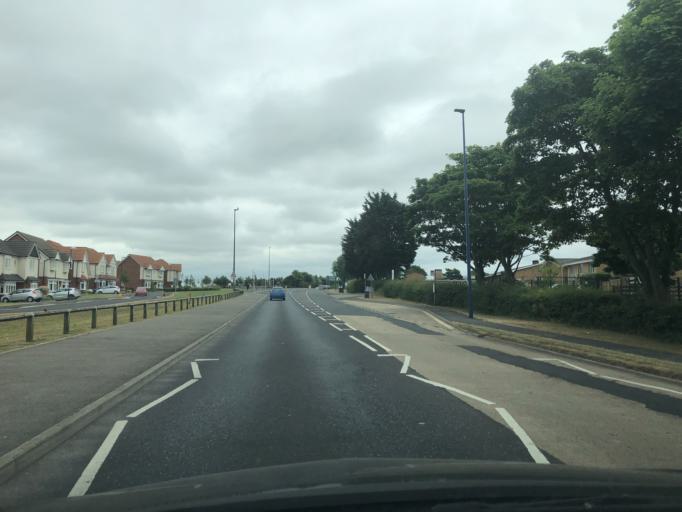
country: GB
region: England
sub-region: North Yorkshire
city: Filey
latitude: 54.2056
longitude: -0.3016
